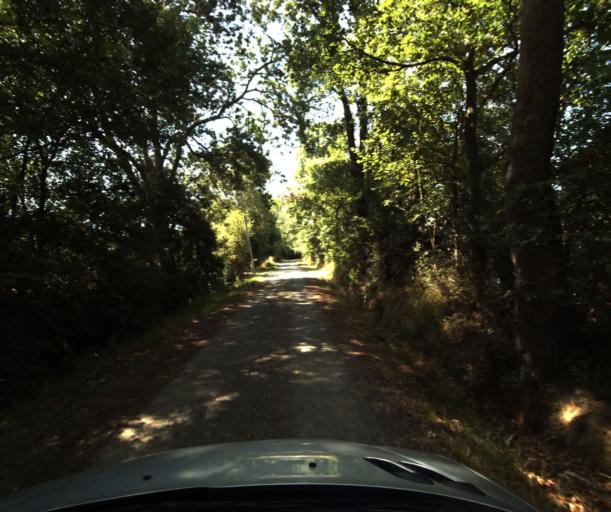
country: FR
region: Midi-Pyrenees
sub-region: Departement de la Haute-Garonne
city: Labastidette
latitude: 43.4666
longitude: 1.2214
